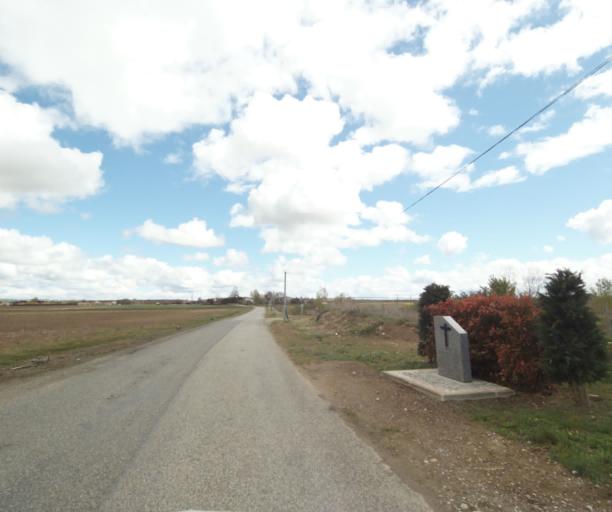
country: FR
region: Midi-Pyrenees
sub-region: Departement de l'Ariege
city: Saverdun
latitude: 43.2377
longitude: 1.6020
